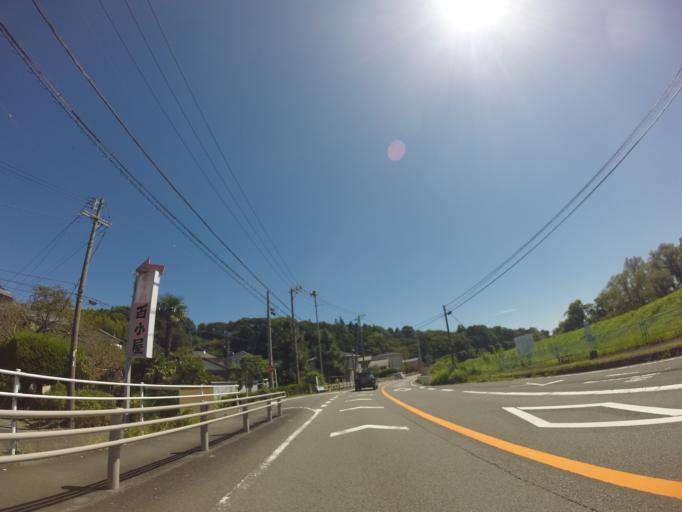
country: JP
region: Shizuoka
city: Kanaya
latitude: 34.8496
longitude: 138.1427
